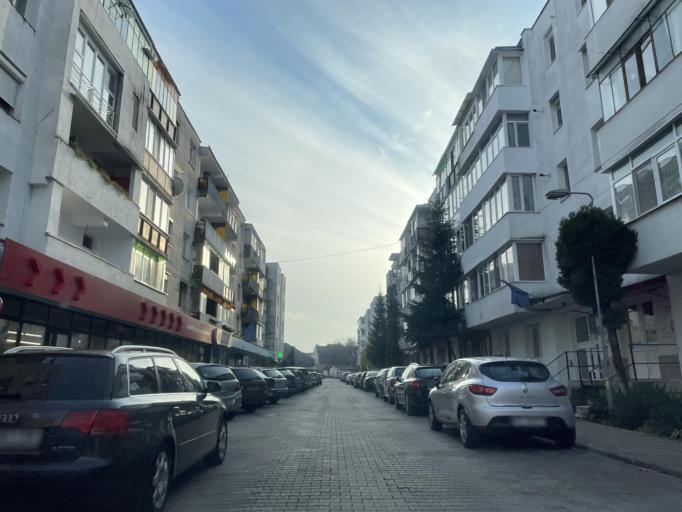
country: RO
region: Mures
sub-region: Municipiul Reghin
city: Reghin
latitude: 46.7832
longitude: 24.6984
